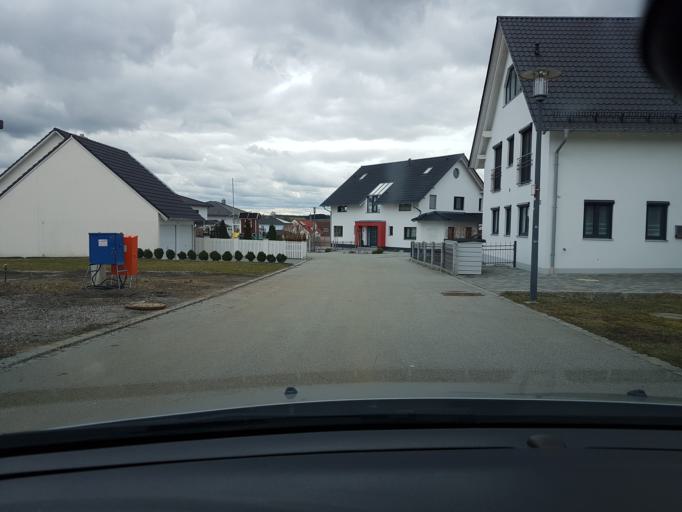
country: DE
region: Bavaria
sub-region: Lower Bavaria
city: Geisenhausen
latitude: 48.4810
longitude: 12.2615
